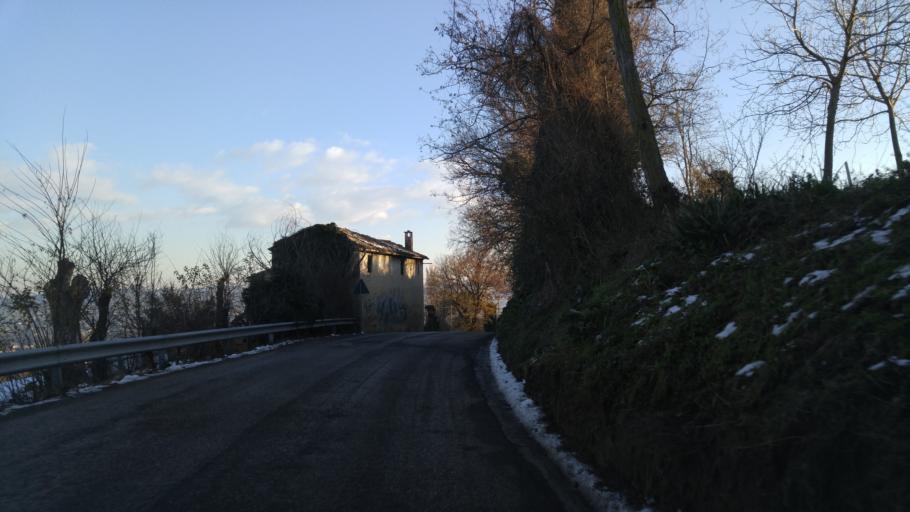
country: IT
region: The Marches
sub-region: Provincia di Pesaro e Urbino
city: San Michele
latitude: 43.6639
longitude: 12.9817
